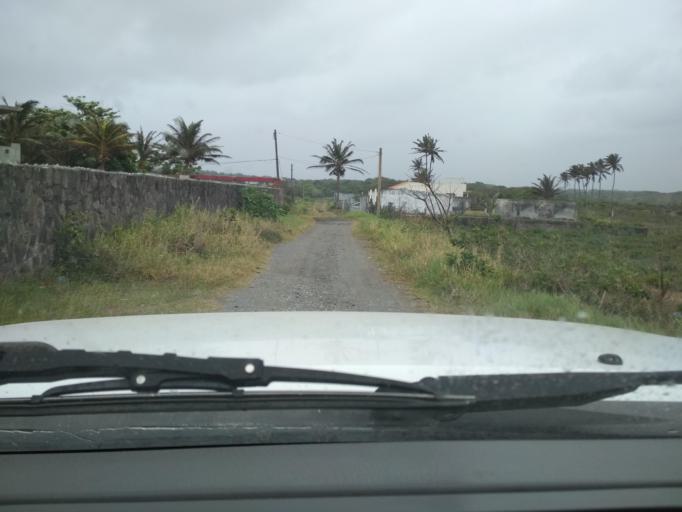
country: MX
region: Veracruz
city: Anton Lizardo
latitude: 19.0572
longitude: -95.9983
